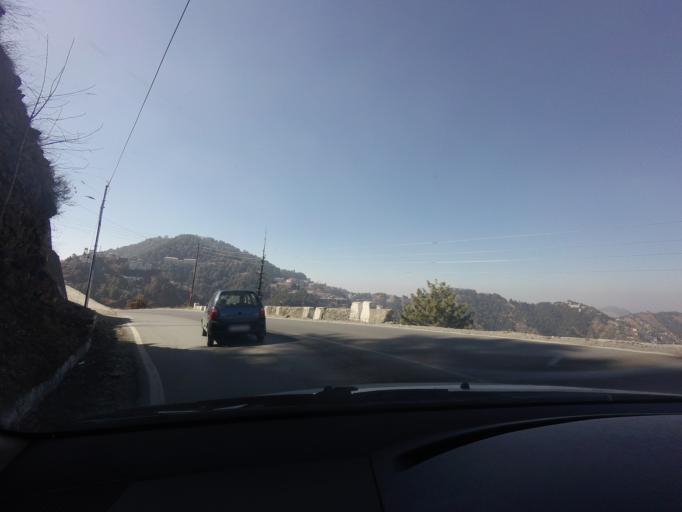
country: IN
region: Himachal Pradesh
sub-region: Shimla
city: Shimla
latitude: 31.1093
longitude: 77.1989
